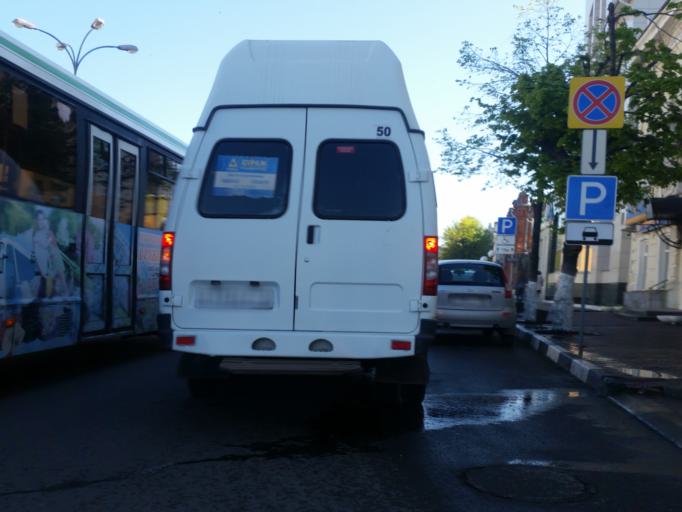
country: RU
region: Ulyanovsk
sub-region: Ulyanovskiy Rayon
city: Ulyanovsk
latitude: 54.3188
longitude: 48.3983
